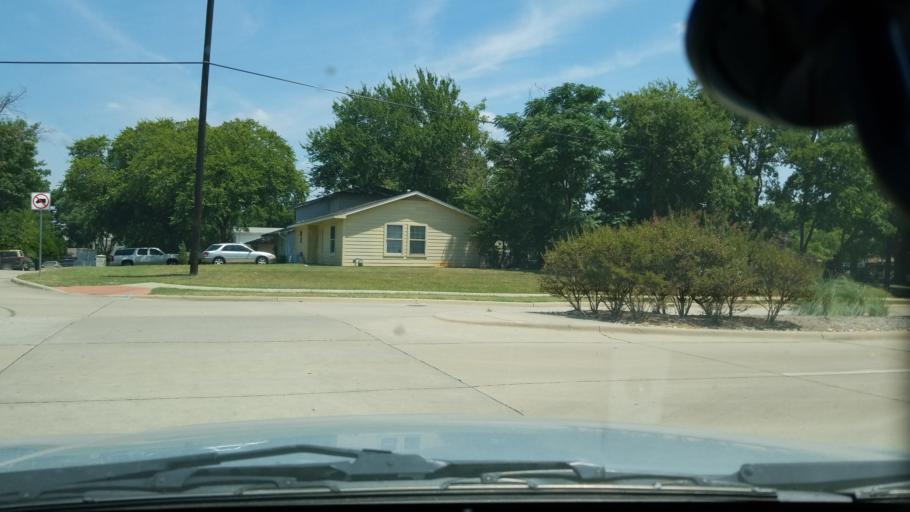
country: US
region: Texas
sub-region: Dallas County
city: Grand Prairie
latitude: 32.7601
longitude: -96.9585
